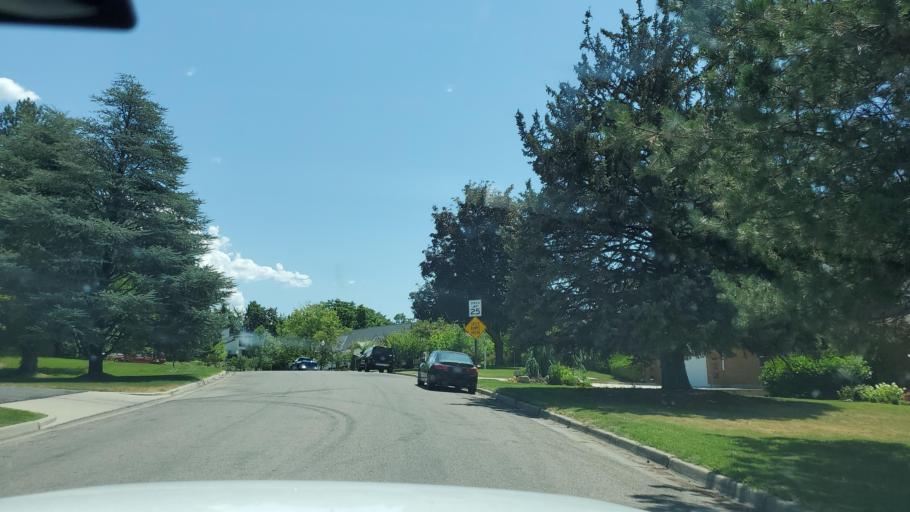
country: US
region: Utah
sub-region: Salt Lake County
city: Willard
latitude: 40.7187
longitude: -111.8309
